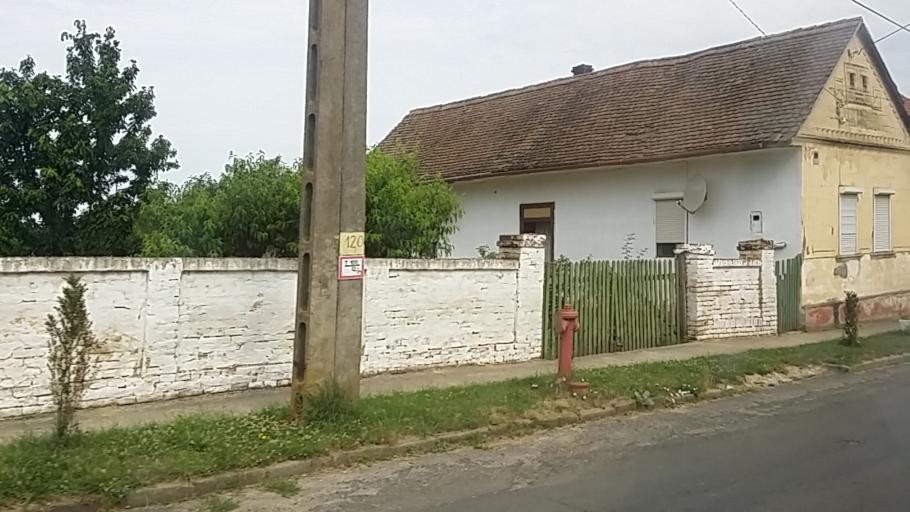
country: HU
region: Baranya
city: Villany
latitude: 45.9082
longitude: 18.4706
